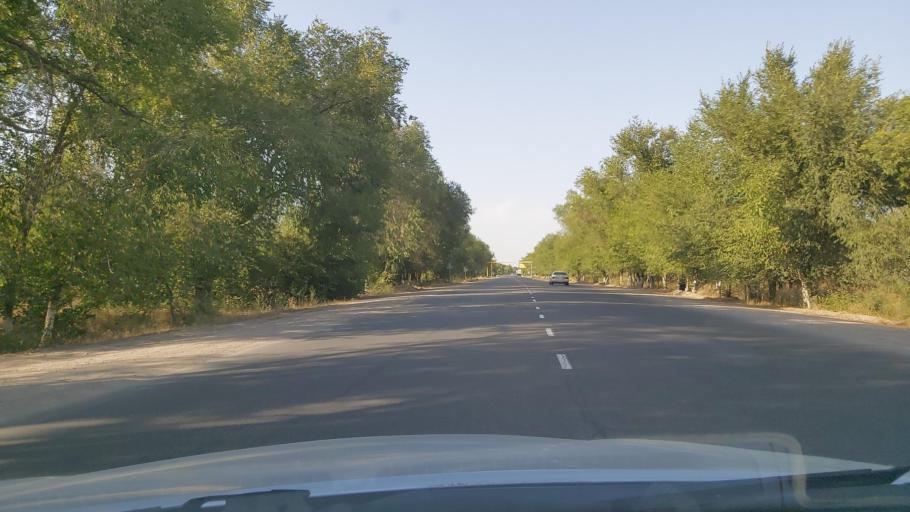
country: KZ
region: Almaty Oblysy
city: Energeticheskiy
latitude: 43.5520
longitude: 77.0529
